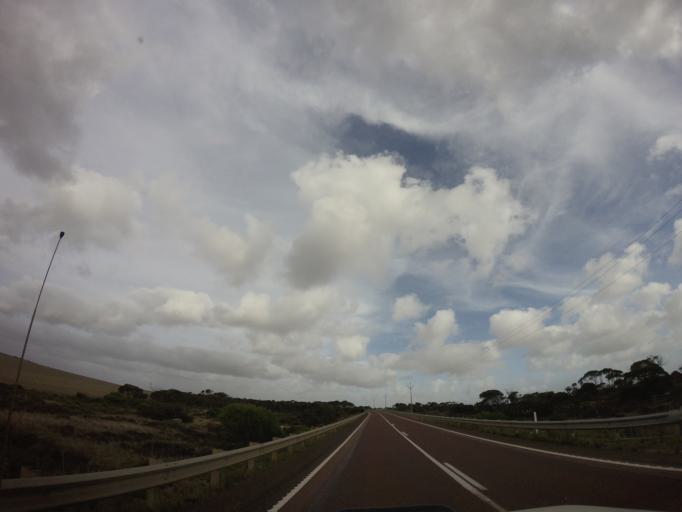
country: AU
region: South Australia
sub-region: Ceduna
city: Ceduna
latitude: -32.0644
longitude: 133.6242
